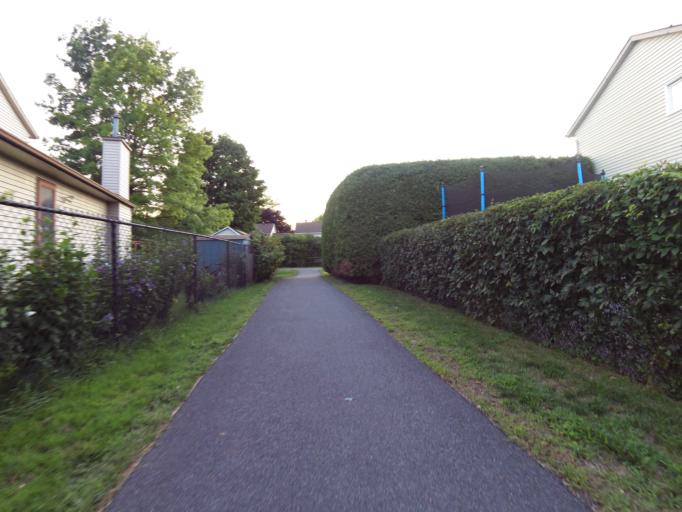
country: CA
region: Quebec
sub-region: Outaouais
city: Gatineau
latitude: 45.4678
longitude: -75.4954
